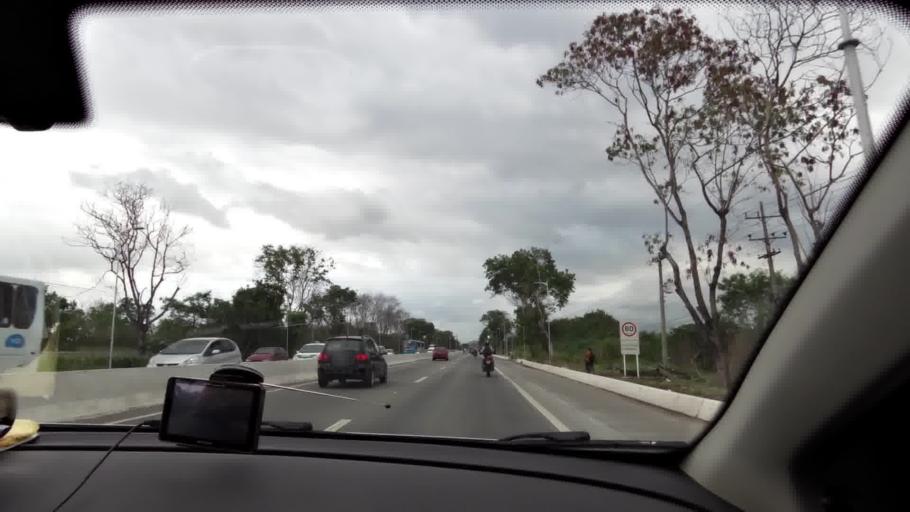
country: BR
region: Espirito Santo
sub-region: Vila Velha
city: Vila Velha
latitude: -20.2475
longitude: -40.2844
